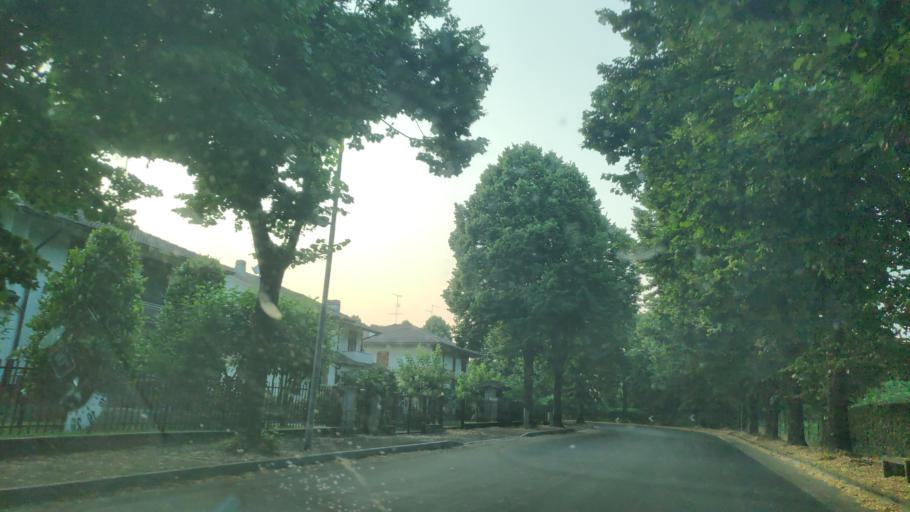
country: IT
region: Lombardy
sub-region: Citta metropolitana di Milano
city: Paullo
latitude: 45.4216
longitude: 9.4084
